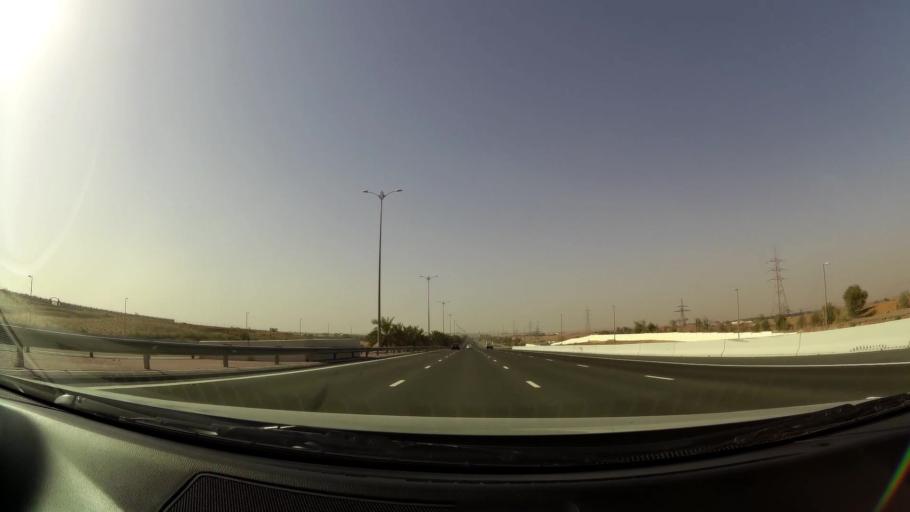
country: OM
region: Al Buraimi
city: Al Buraymi
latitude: 24.4864
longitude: 55.7729
